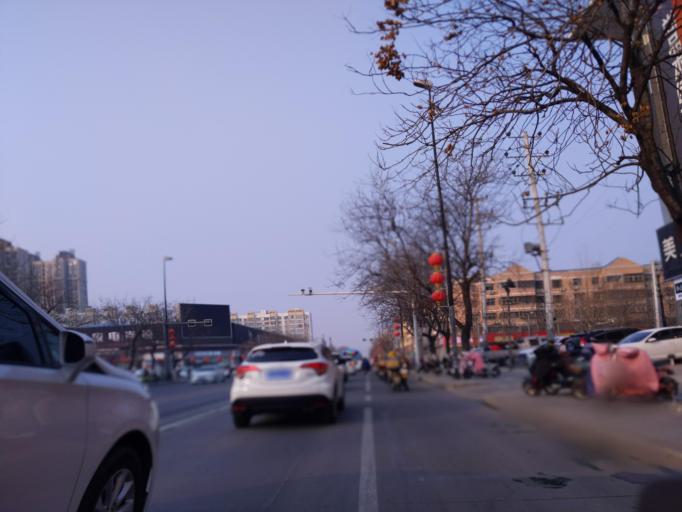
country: CN
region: Henan Sheng
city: Zhongyuanlu
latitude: 35.7739
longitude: 115.0596
